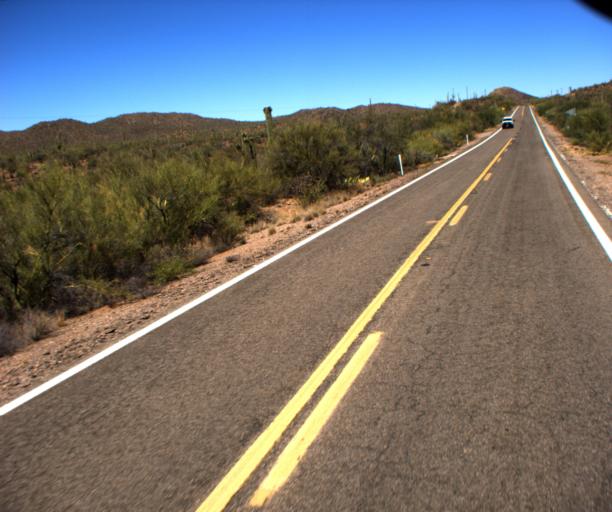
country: US
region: Arizona
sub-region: Pima County
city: Sells
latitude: 32.1692
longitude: -112.1389
